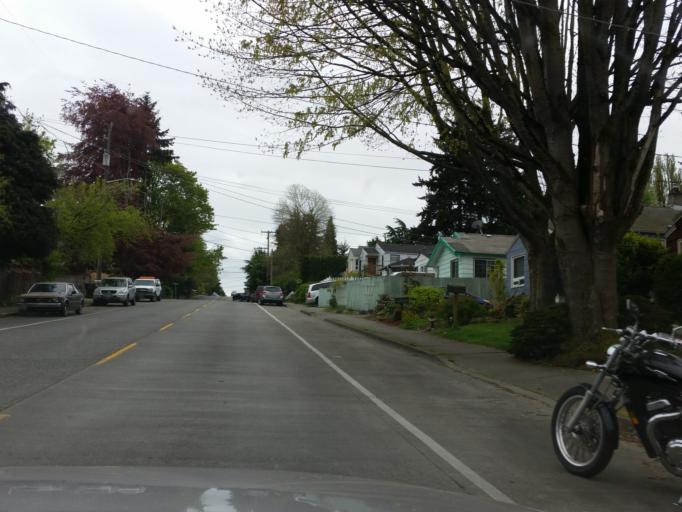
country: US
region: Washington
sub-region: King County
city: Shoreline
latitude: 47.6974
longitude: -122.3661
